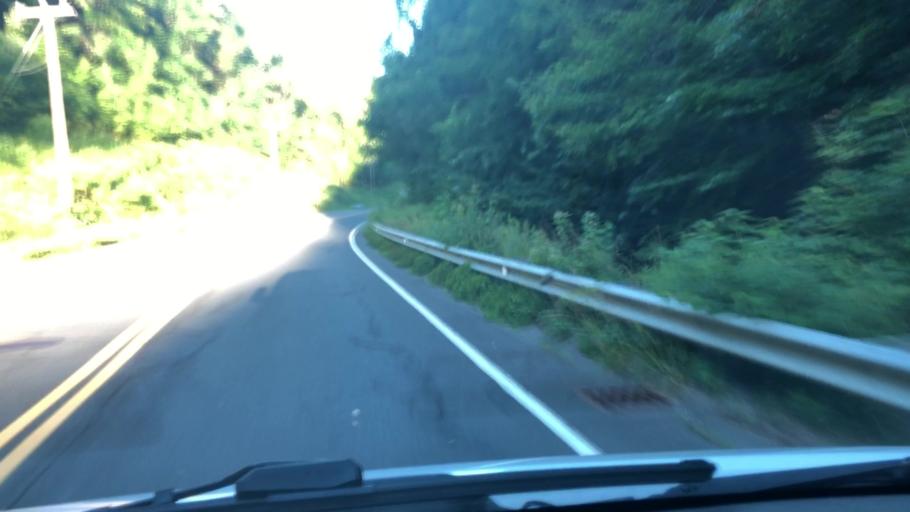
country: US
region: Massachusetts
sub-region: Hampshire County
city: Westhampton
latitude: 42.2838
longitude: -72.8471
